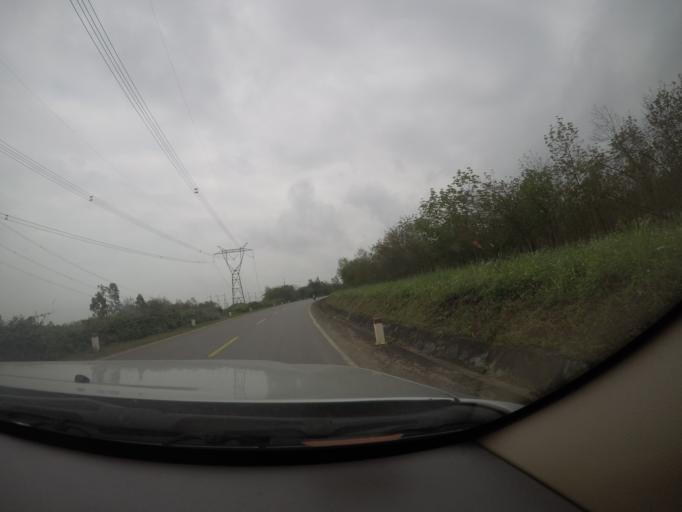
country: VN
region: Quang Binh
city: Hoan Lao
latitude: 17.5449
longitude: 106.4649
